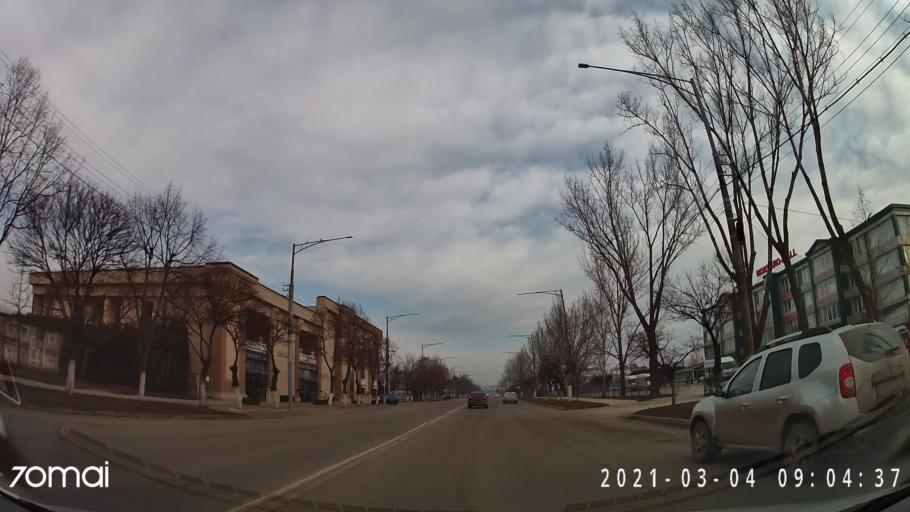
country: MD
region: Balti
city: Balti
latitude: 47.7593
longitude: 27.9409
